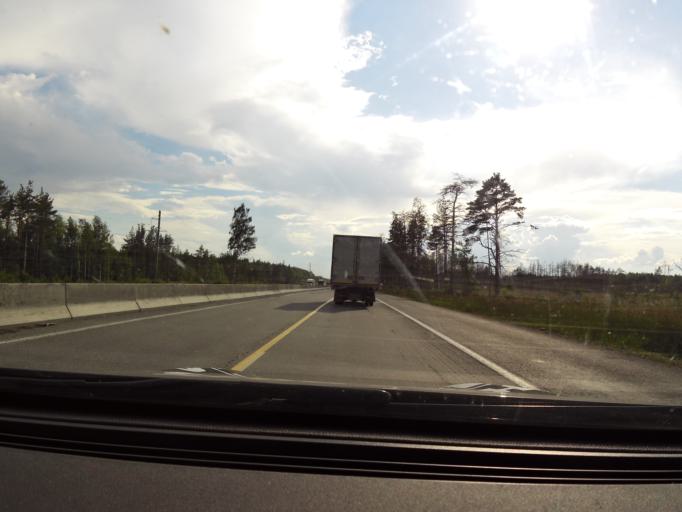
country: RU
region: Nizjnij Novgorod
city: Mulino
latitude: 56.2590
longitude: 42.9085
